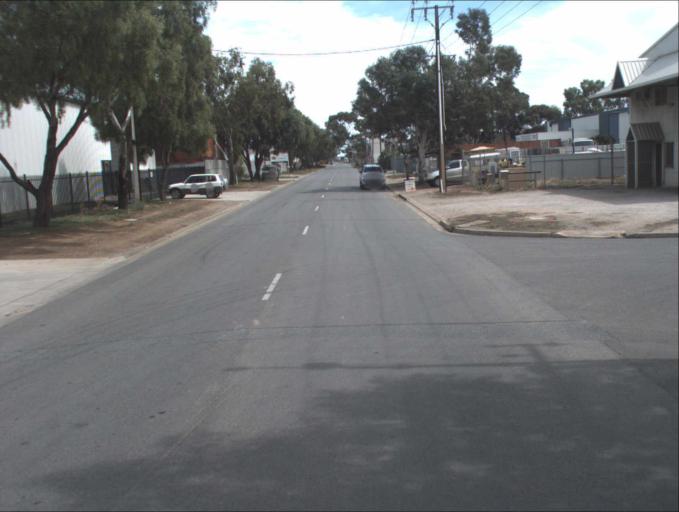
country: AU
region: South Australia
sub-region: Charles Sturt
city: Woodville North
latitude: -34.8392
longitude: 138.5549
